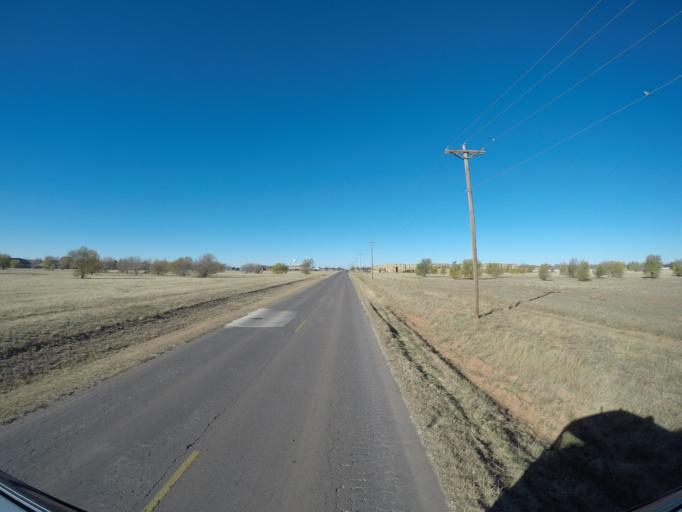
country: US
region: New Mexico
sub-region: Curry County
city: Clovis
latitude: 34.4339
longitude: -103.1711
